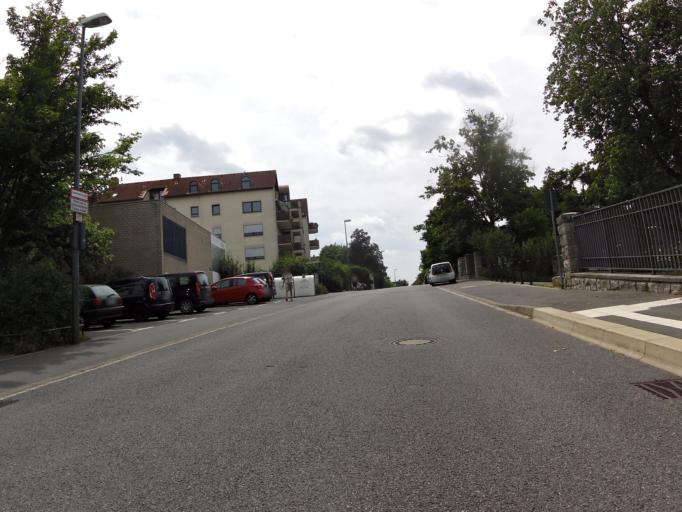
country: DE
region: Bavaria
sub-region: Regierungsbezirk Unterfranken
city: Wuerzburg
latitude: 49.7933
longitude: 9.9579
